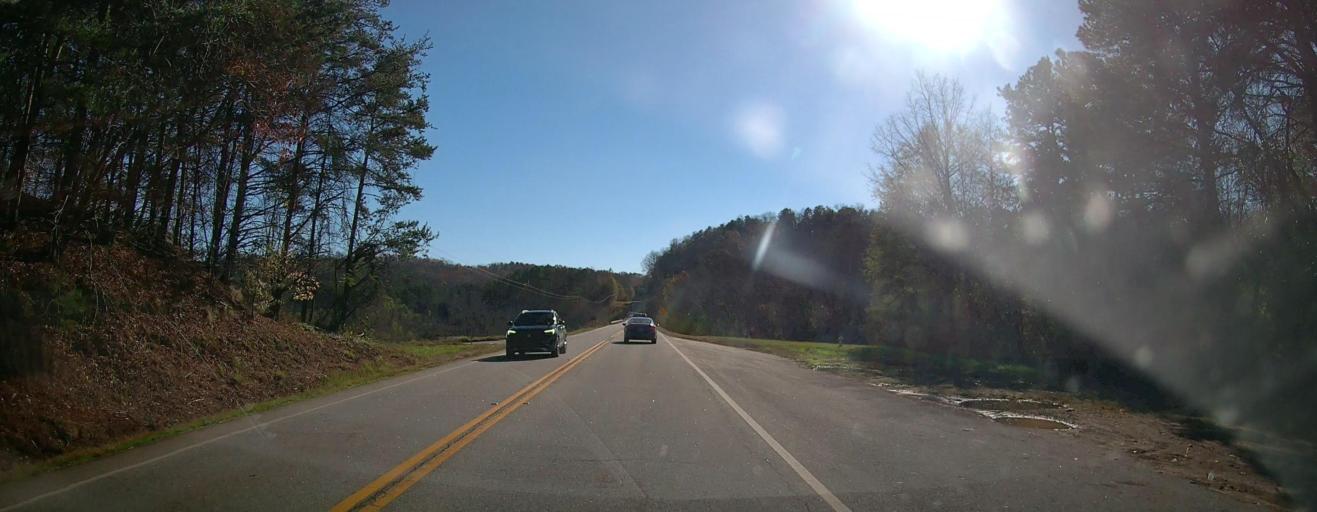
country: US
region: Georgia
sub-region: Hall County
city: Lula
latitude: 34.4164
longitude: -83.7079
